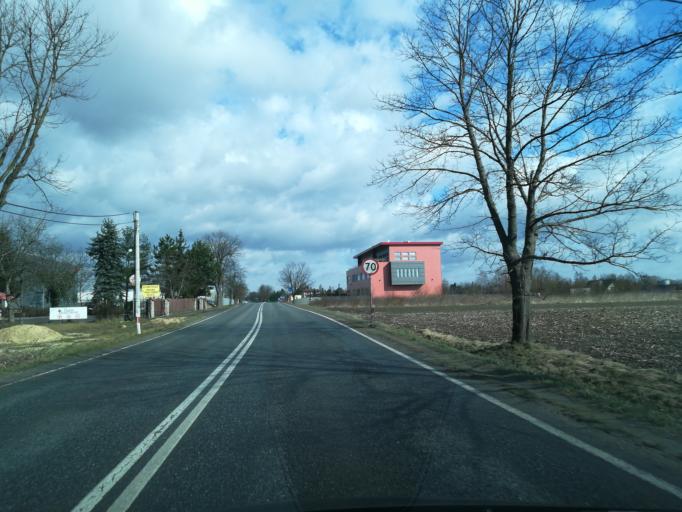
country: PL
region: Lesser Poland Voivodeship
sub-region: Powiat krakowski
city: Kryspinow
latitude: 50.0566
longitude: 19.8025
